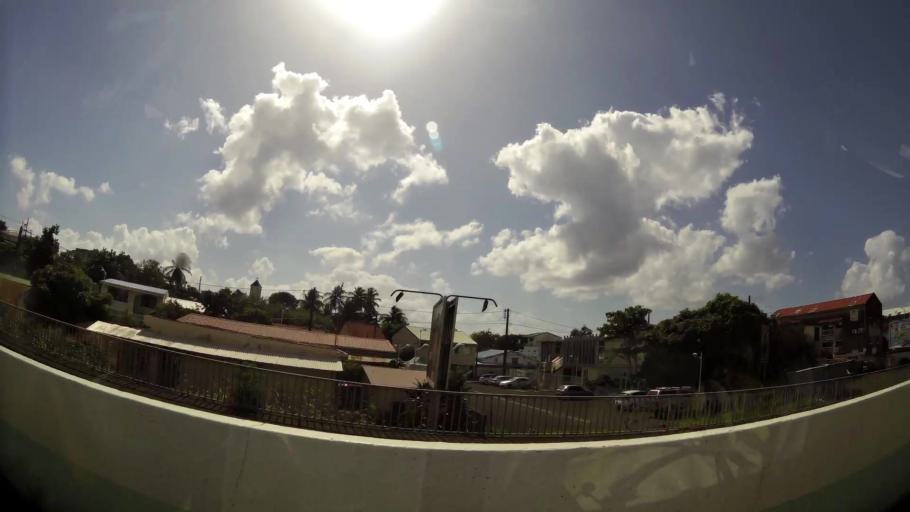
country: MQ
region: Martinique
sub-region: Martinique
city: Fort-de-France
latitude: 14.6180
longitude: -61.1012
